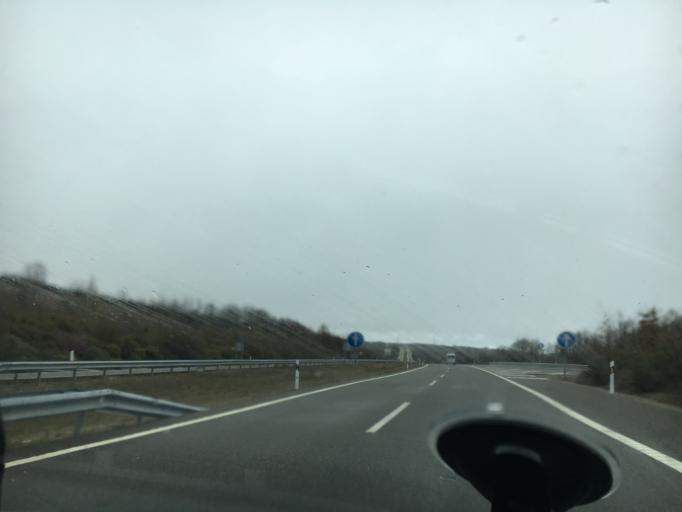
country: ES
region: Castille and Leon
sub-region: Provincia de Zamora
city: Puebla de Sanabria
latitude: 42.0561
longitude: -6.6052
